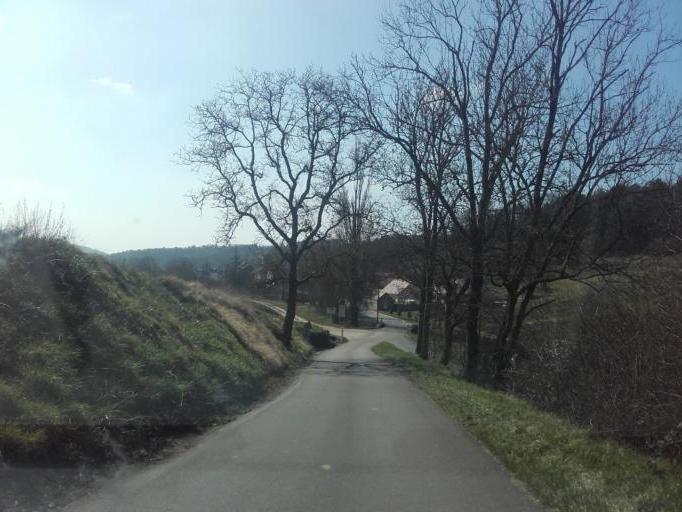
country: FR
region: Bourgogne
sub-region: Departement de la Cote-d'Or
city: Meursault
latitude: 47.0379
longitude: 4.7607
